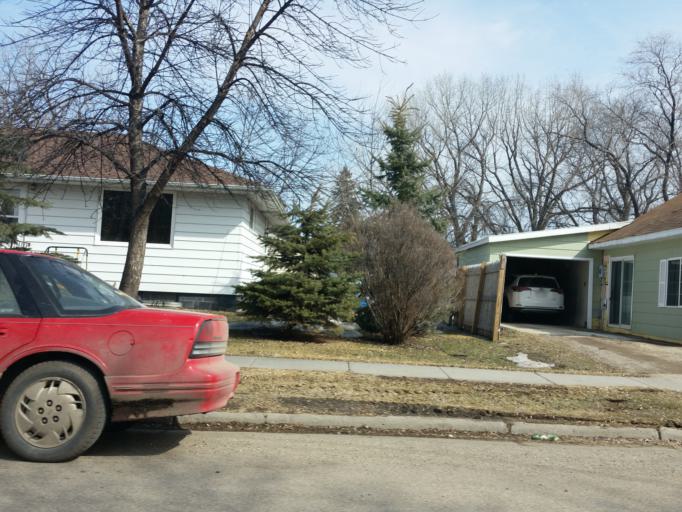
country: US
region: North Dakota
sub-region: Walsh County
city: Grafton
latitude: 48.4161
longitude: -97.4025
